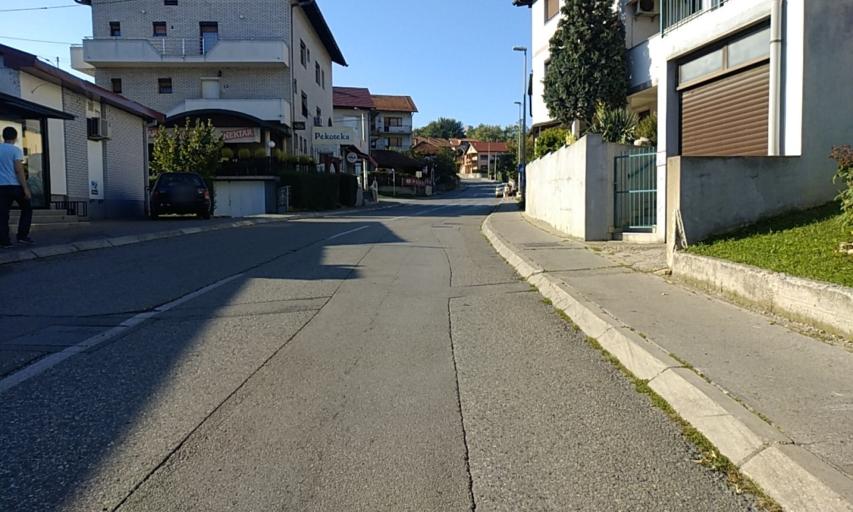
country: BA
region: Republika Srpska
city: Banja Luka
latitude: 44.7796
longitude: 17.1824
